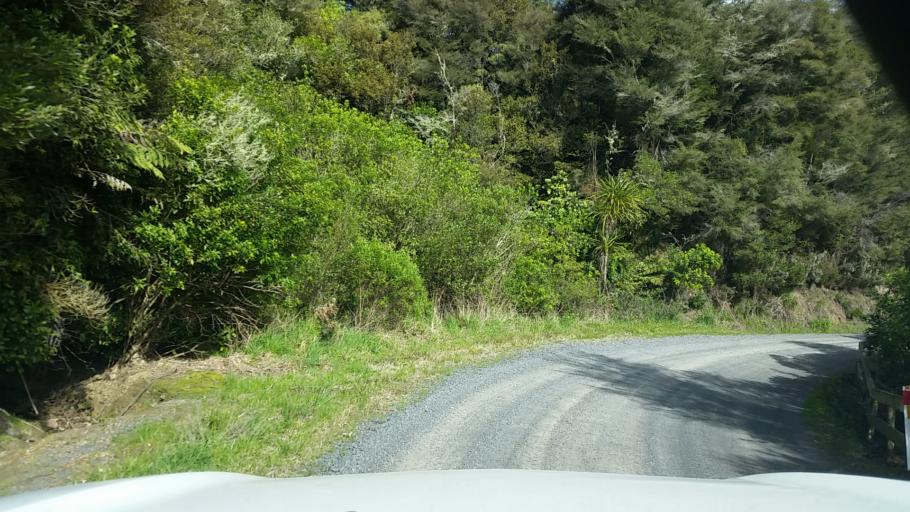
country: NZ
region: Waikato
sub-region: Hauraki District
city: Ngatea
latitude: -37.4776
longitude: 175.4552
